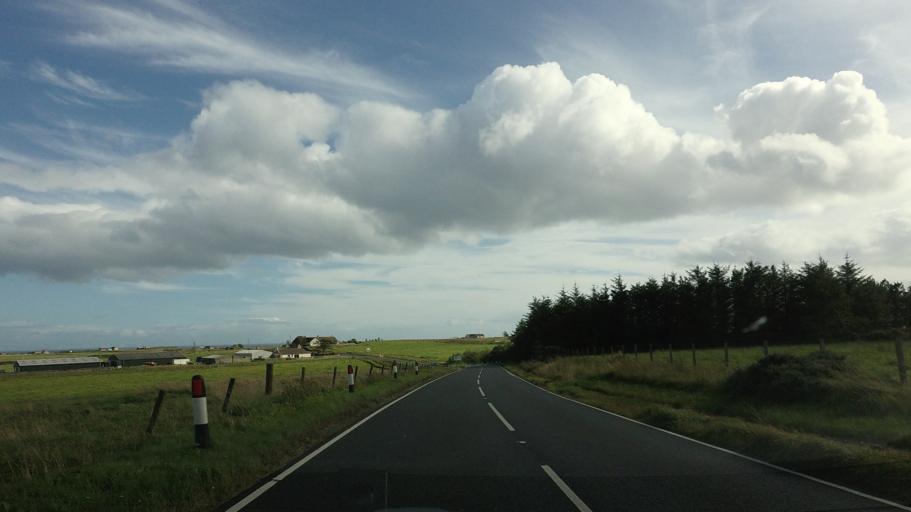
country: GB
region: Scotland
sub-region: Highland
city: Wick
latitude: 58.3082
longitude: -3.2622
